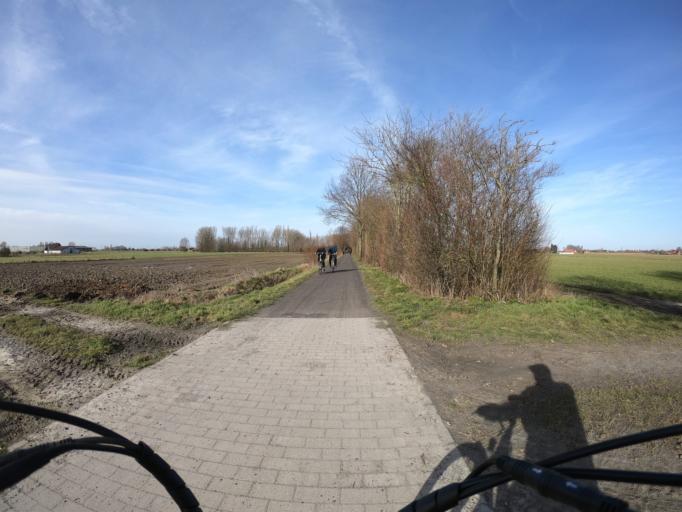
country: BE
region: Flanders
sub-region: Provincie West-Vlaanderen
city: Ledegem
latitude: 50.8827
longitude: 3.1271
